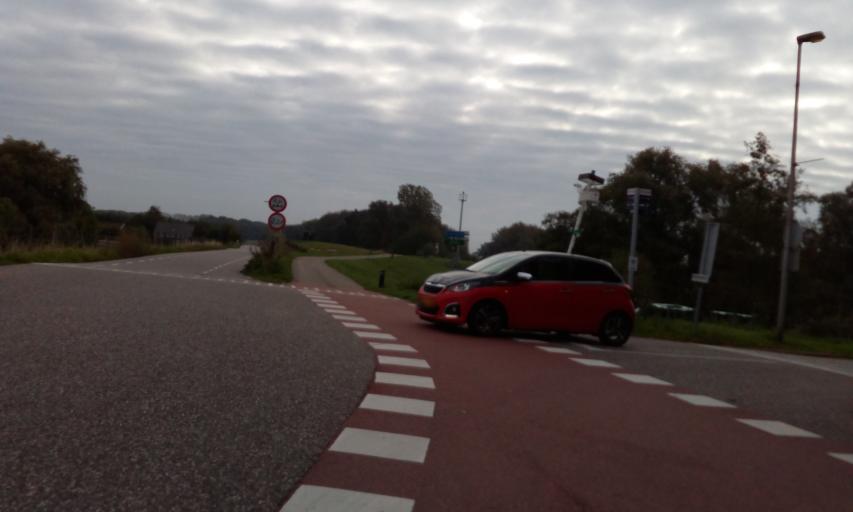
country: NL
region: South Holland
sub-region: Gemeente Albrandswaard
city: Rhoon
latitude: 51.8474
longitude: 4.4031
